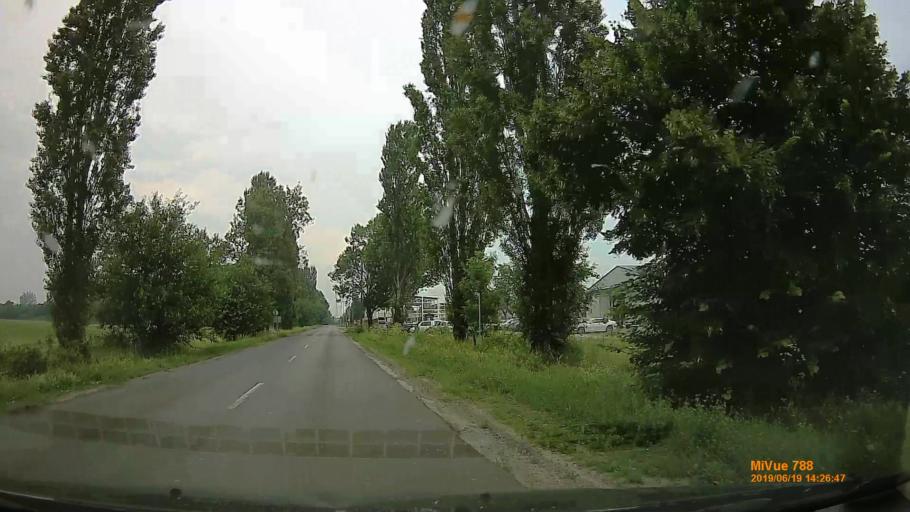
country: HU
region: Baranya
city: Szigetvar
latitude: 46.0359
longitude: 17.7814
